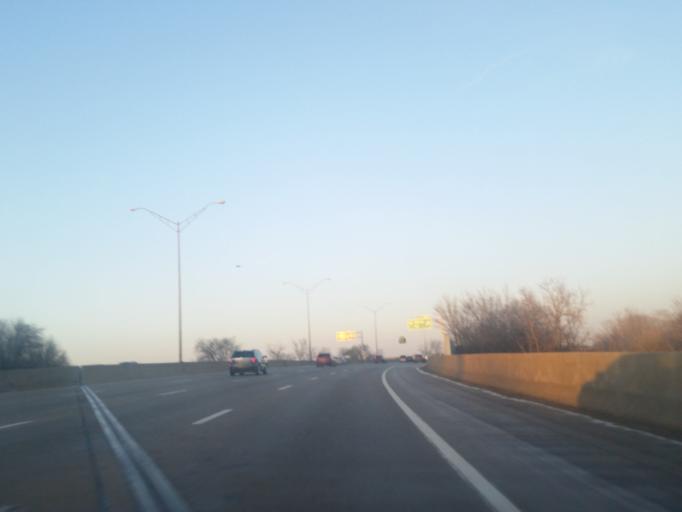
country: US
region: Ohio
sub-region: Cuyahoga County
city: Brook Park
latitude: 41.4374
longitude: -81.8091
